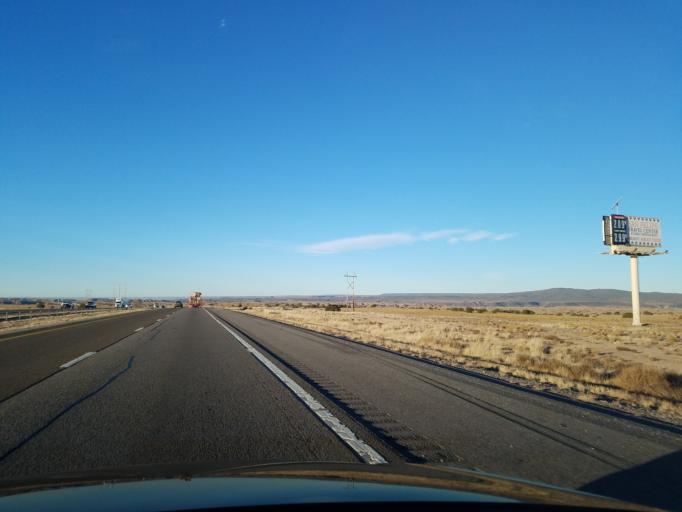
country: US
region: New Mexico
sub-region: Sandoval County
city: Santo Domingo Pueblo
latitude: 35.4493
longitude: -106.3557
